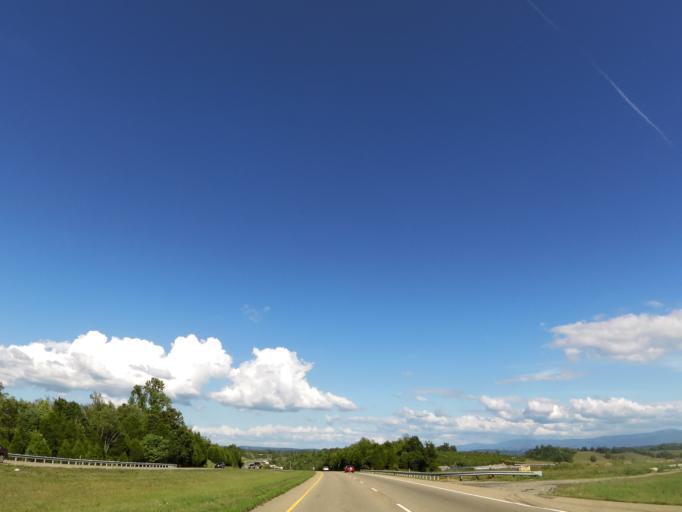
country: US
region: Tennessee
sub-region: Greene County
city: Mosheim
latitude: 36.1869
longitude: -82.9711
